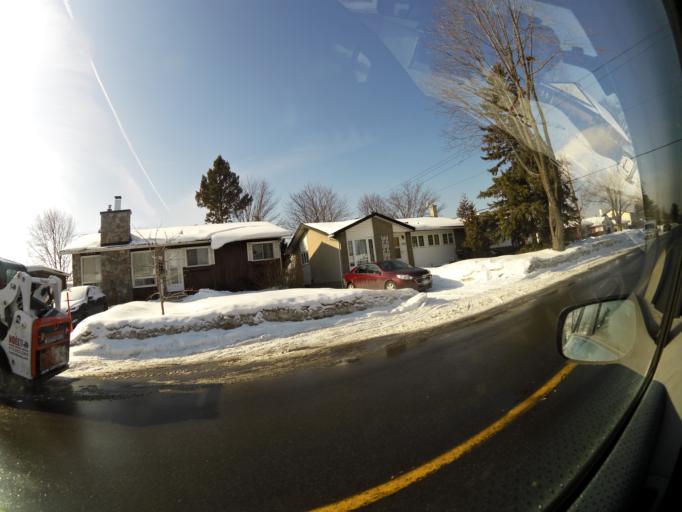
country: CA
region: Ontario
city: Ottawa
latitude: 45.3904
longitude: -75.6352
